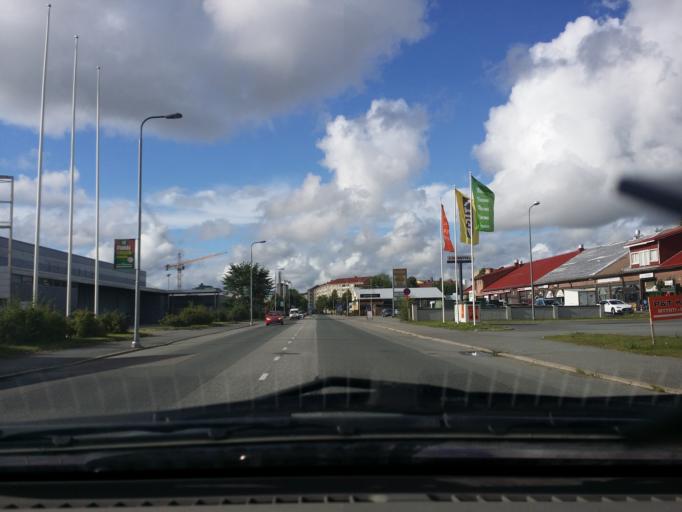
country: FI
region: Satakunta
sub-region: Pori
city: Pori
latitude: 61.4748
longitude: 21.7967
